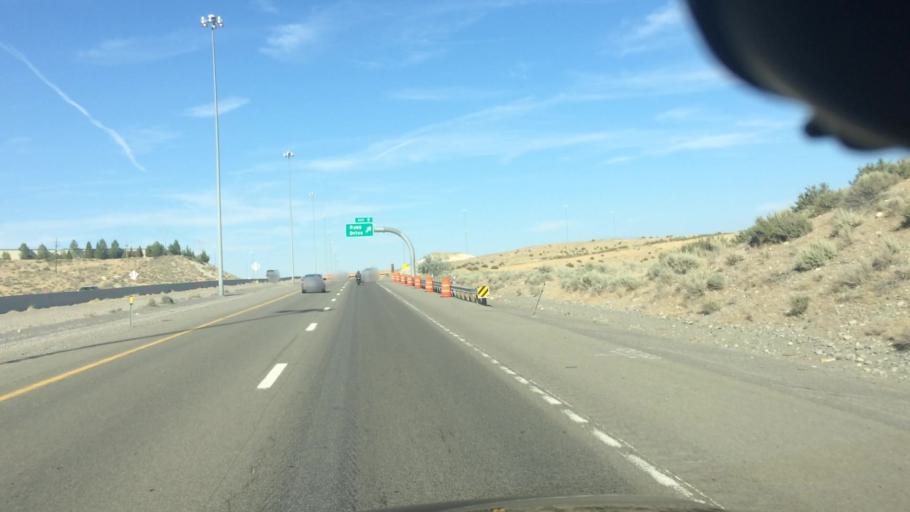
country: US
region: Nevada
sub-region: Washoe County
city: Mogul
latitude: 39.5145
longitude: -119.8950
